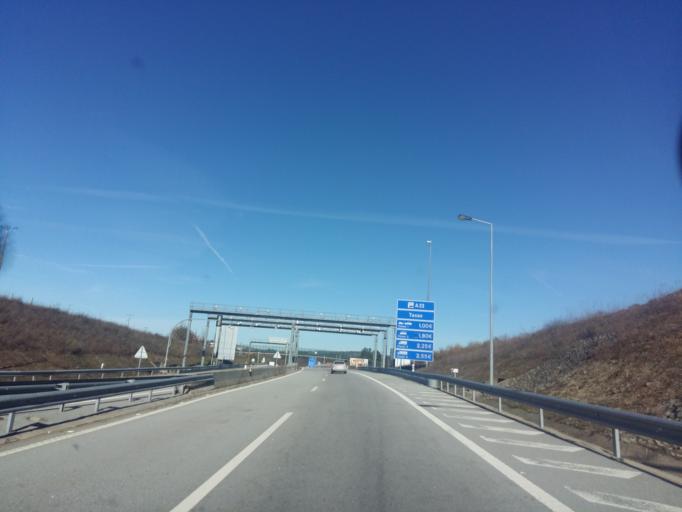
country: PT
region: Guarda
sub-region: Guarda
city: Guarda
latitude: 40.5079
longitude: -7.2357
